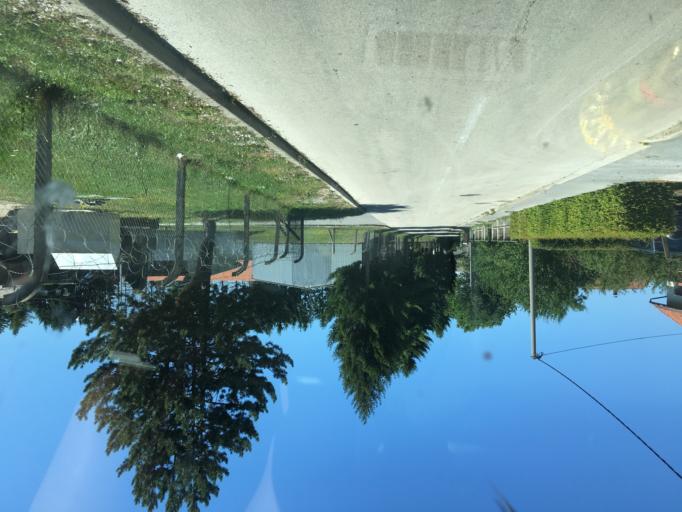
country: HR
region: Licko-Senjska
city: Gospic
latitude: 44.5487
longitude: 15.3590
